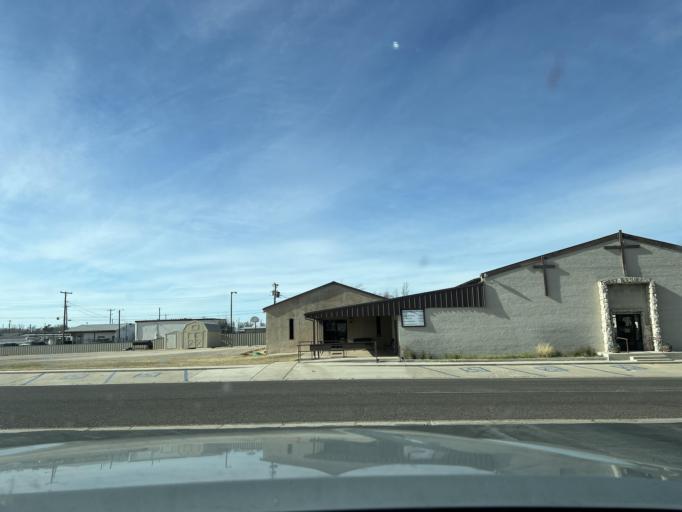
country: US
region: Texas
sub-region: Andrews County
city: Andrews
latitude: 32.3176
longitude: -102.5549
